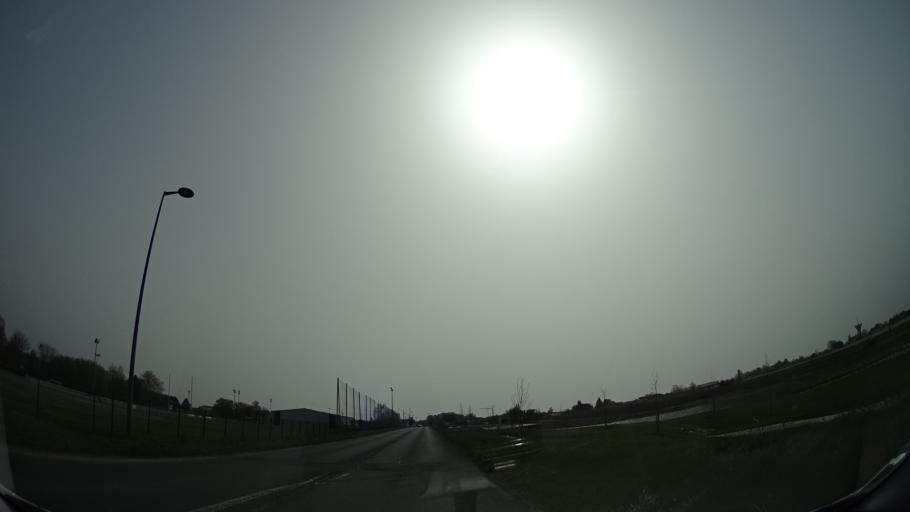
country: FR
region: Pays de la Loire
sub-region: Departement de Maine-et-Loire
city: Doue-la-Fontaine
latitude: 47.2029
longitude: -0.2861
